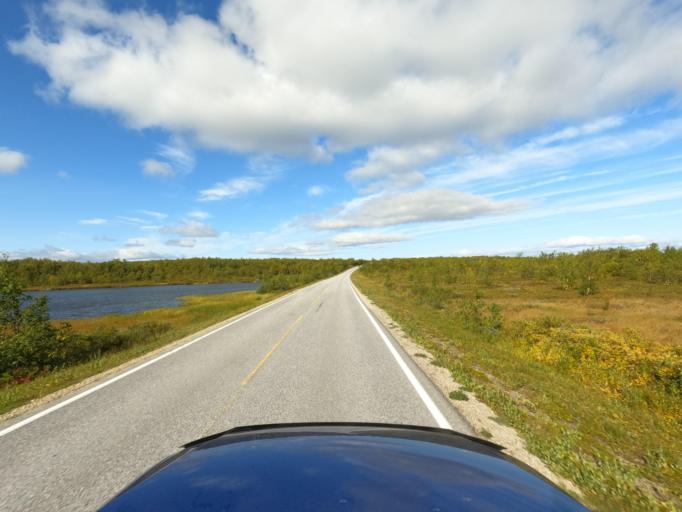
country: NO
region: Finnmark Fylke
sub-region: Karasjok
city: Karasjohka
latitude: 69.6126
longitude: 25.3054
